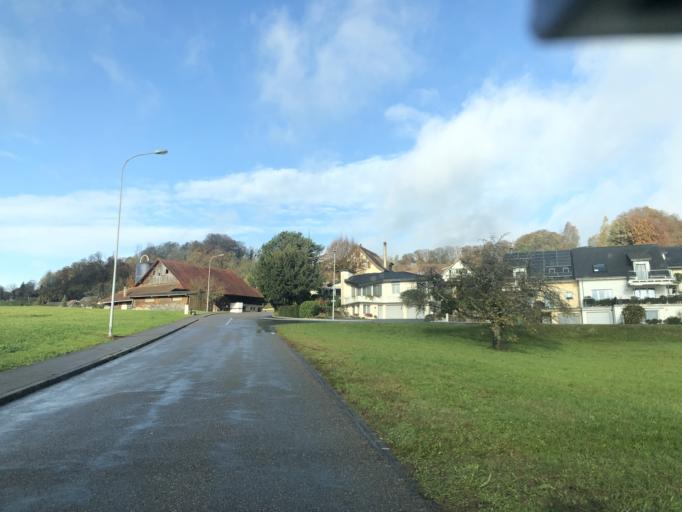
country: CH
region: Aargau
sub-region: Bezirk Baden
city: Unterehrendingen
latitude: 47.5208
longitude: 8.3602
